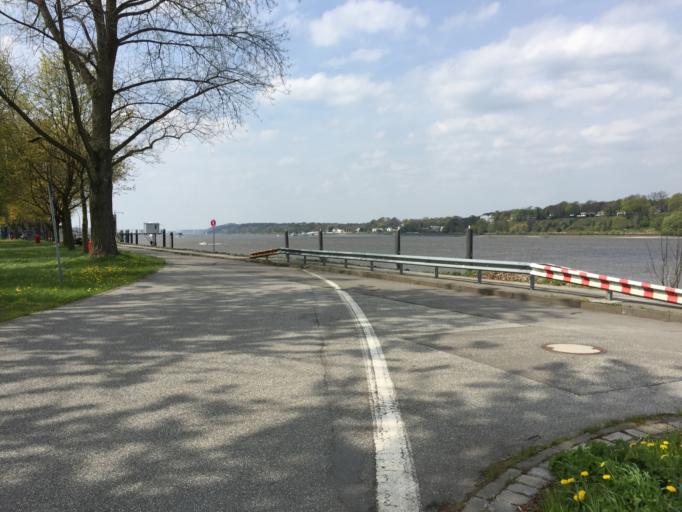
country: DE
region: Hamburg
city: Altona
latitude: 53.5398
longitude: 9.8833
